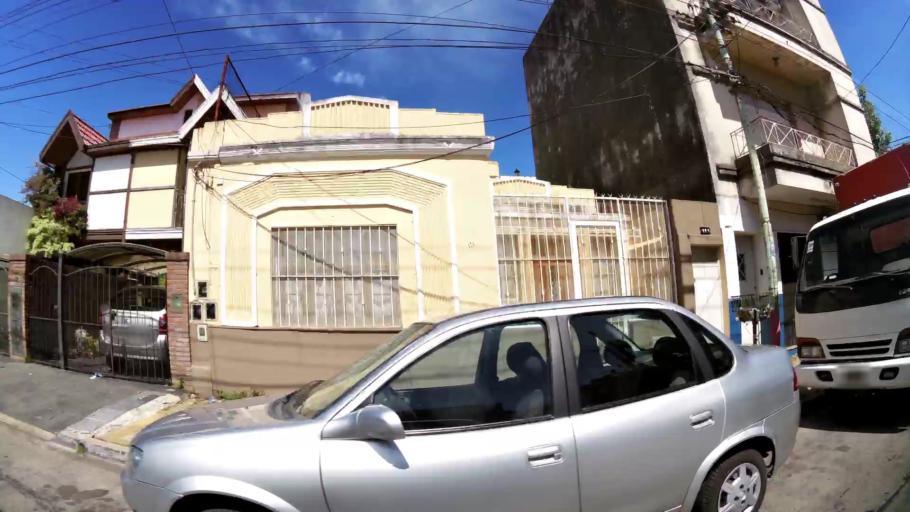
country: AR
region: Buenos Aires
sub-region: Partido de Quilmes
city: Quilmes
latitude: -34.7143
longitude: -58.2618
